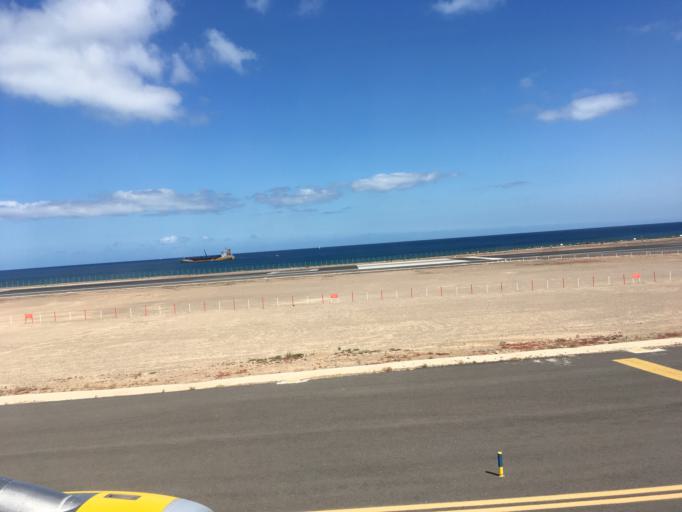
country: ES
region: Canary Islands
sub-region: Provincia de Las Palmas
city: Tias
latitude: 28.9377
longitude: -13.6119
